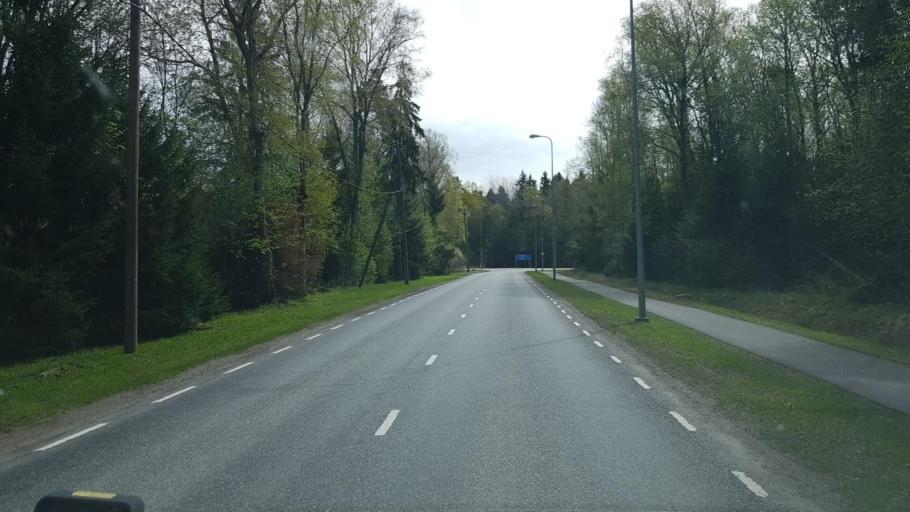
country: EE
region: Harju
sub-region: Viimsi vald
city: Viimsi
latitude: 59.5463
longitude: 24.8583
